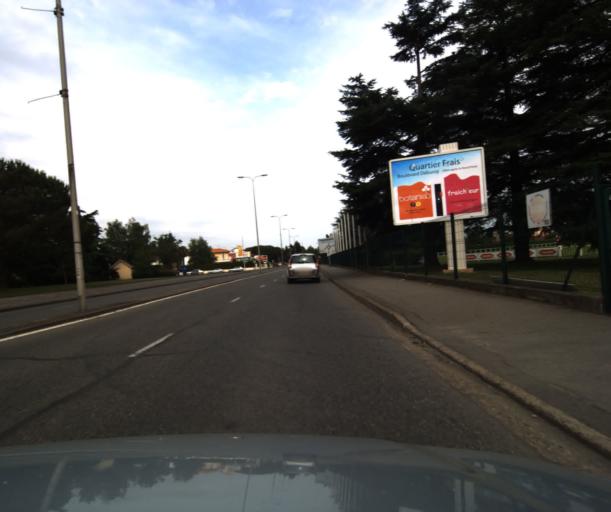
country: FR
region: Midi-Pyrenees
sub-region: Departement des Hautes-Pyrenees
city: Laloubere
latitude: 43.2188
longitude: 0.0738
